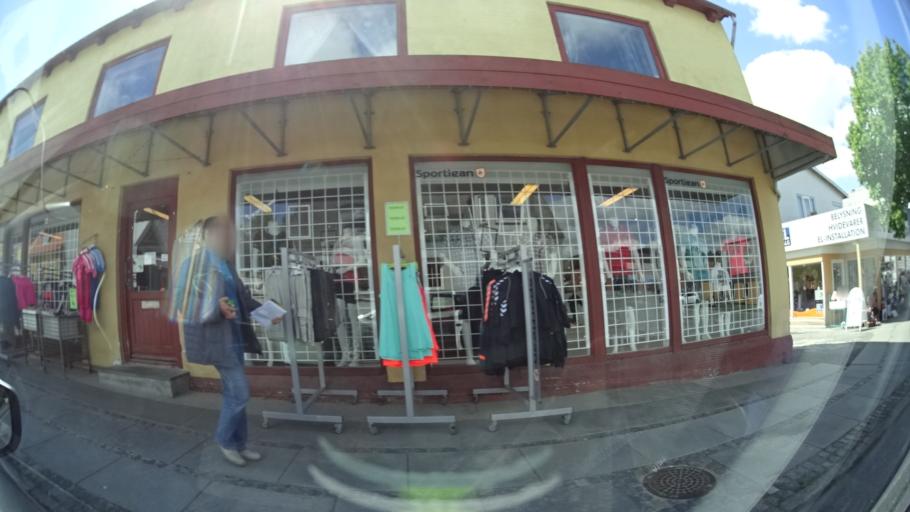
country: DK
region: Central Jutland
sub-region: Syddjurs Kommune
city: Ronde
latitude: 56.3001
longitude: 10.4787
